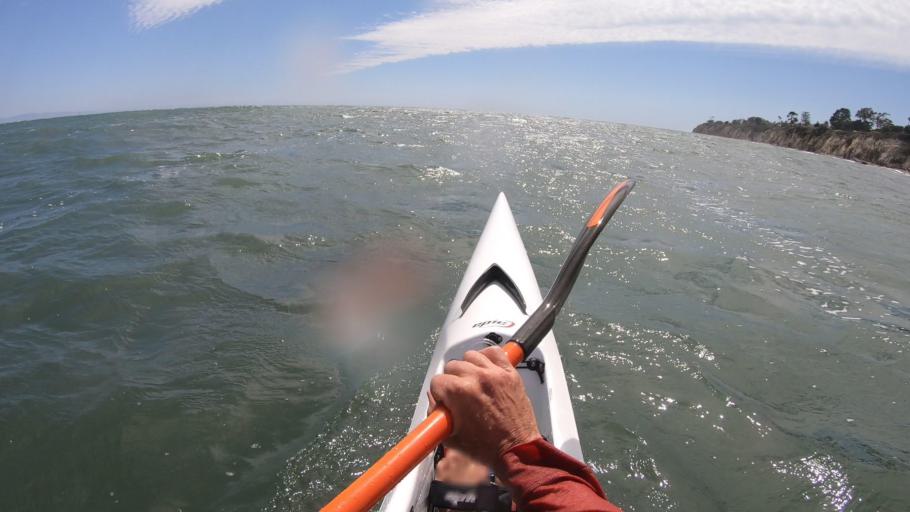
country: US
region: California
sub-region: Santa Barbara County
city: Santa Barbara
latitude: 34.3951
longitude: -119.6998
